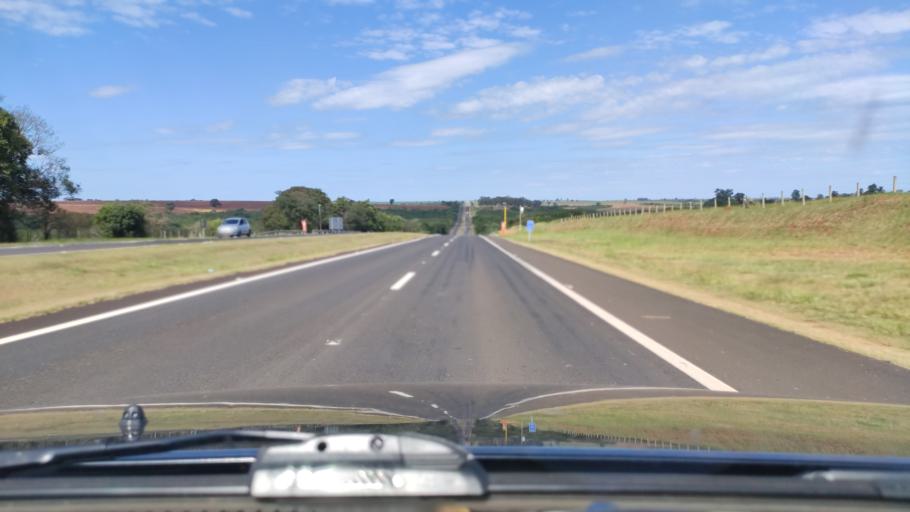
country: BR
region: Sao Paulo
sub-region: Rancharia
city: Rancharia
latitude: -22.4839
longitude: -50.9250
